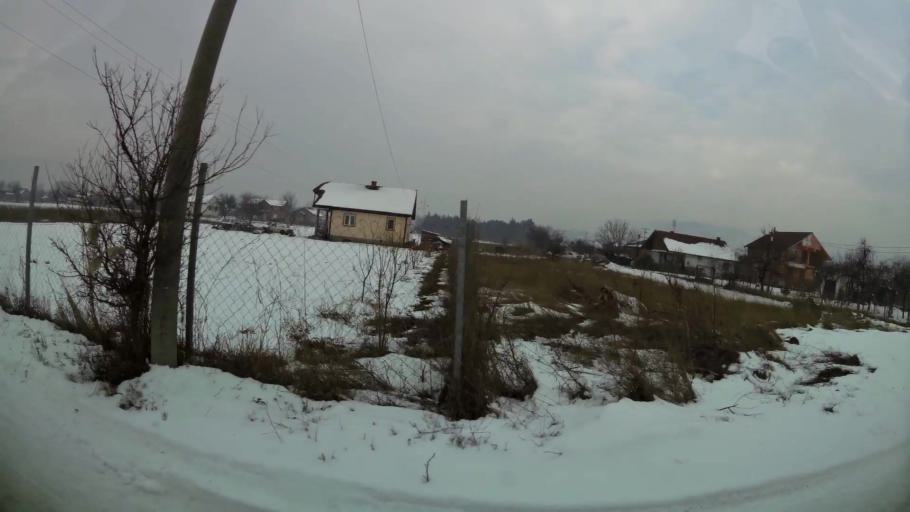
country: MK
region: Saraj
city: Saraj
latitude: 42.0411
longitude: 21.3579
